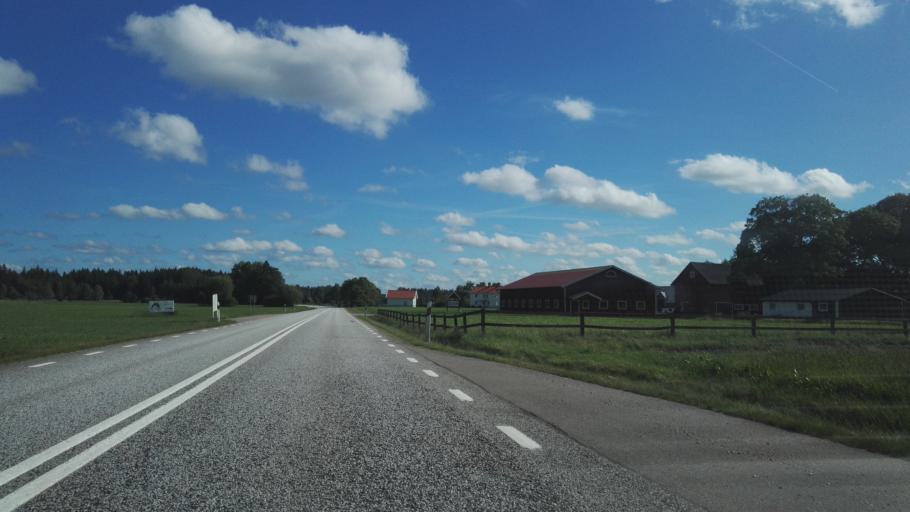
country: SE
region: Joenkoeping
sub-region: Savsjo Kommun
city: Vrigstad
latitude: 57.3347
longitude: 14.4693
